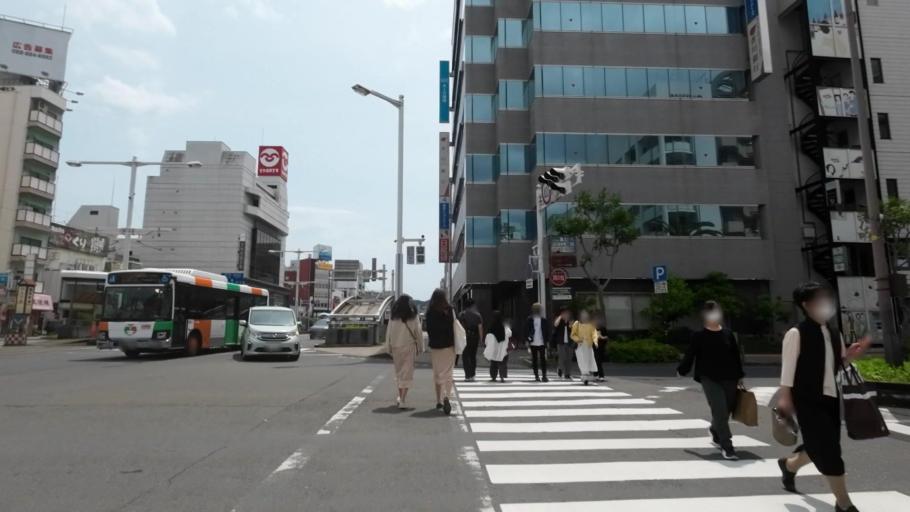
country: JP
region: Kochi
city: Kochi-shi
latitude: 33.5623
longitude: 133.5431
